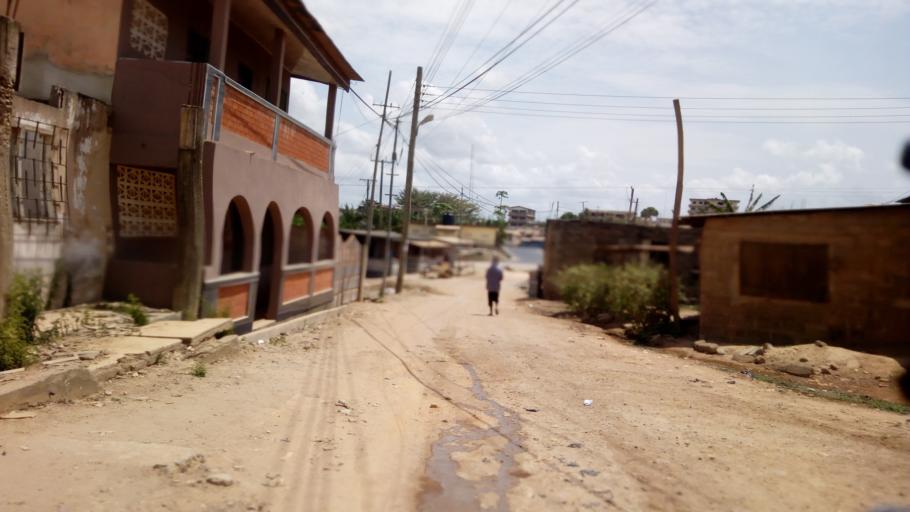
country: GH
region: Central
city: Cape Coast
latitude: 5.1258
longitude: -1.2737
